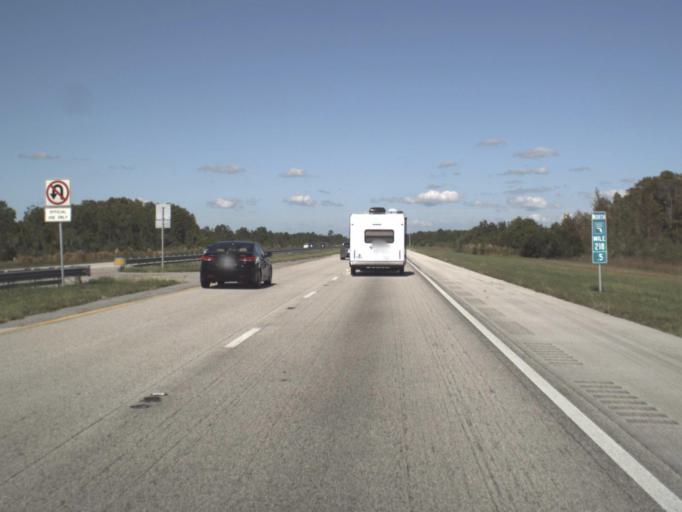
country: US
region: Florida
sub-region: Osceola County
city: Saint Cloud
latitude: 27.9891
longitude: -81.1269
